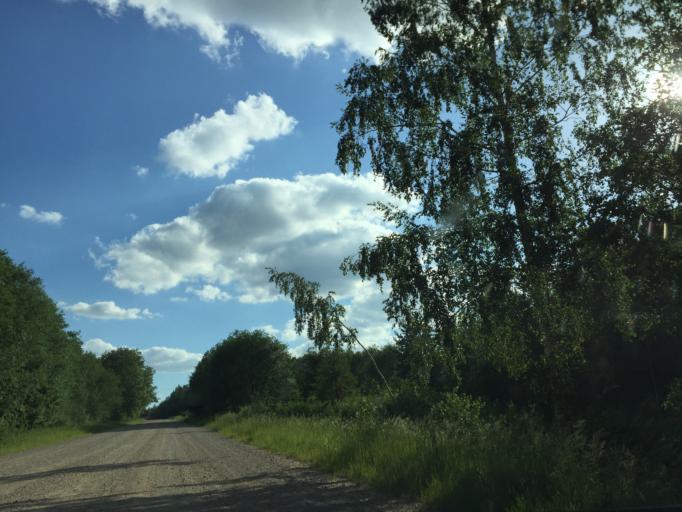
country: LV
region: Kandava
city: Kandava
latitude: 56.8693
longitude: 22.7646
